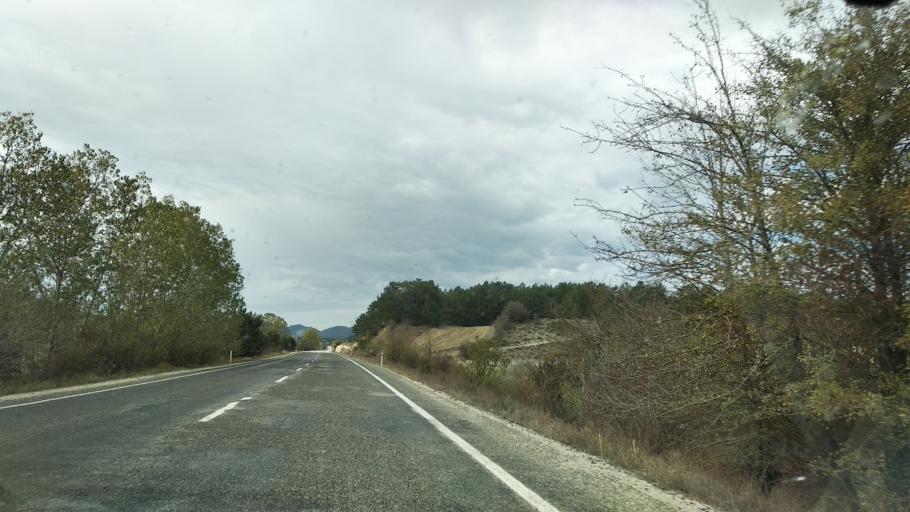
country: TR
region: Bolu
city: Mudurnu
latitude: 40.3950
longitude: 31.2064
